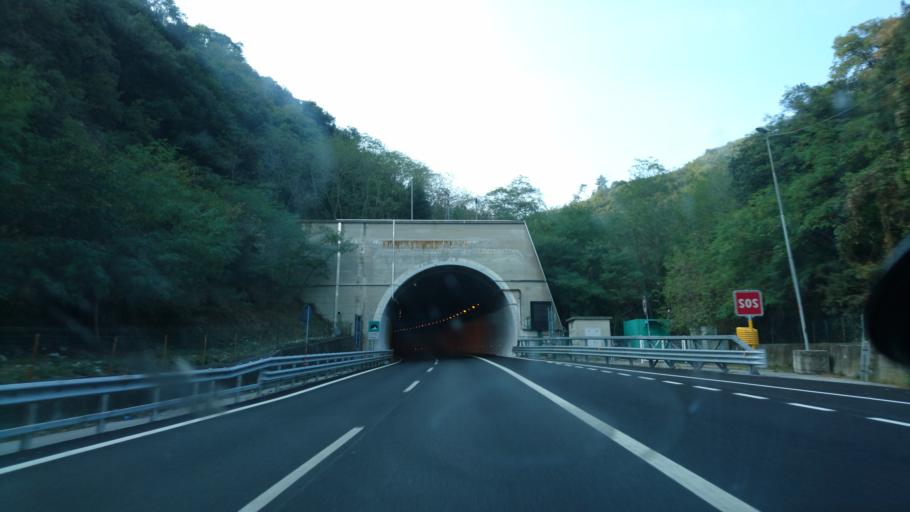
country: IT
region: Liguria
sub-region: Provincia di Savona
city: Quiliano
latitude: 44.2998
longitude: 8.4253
